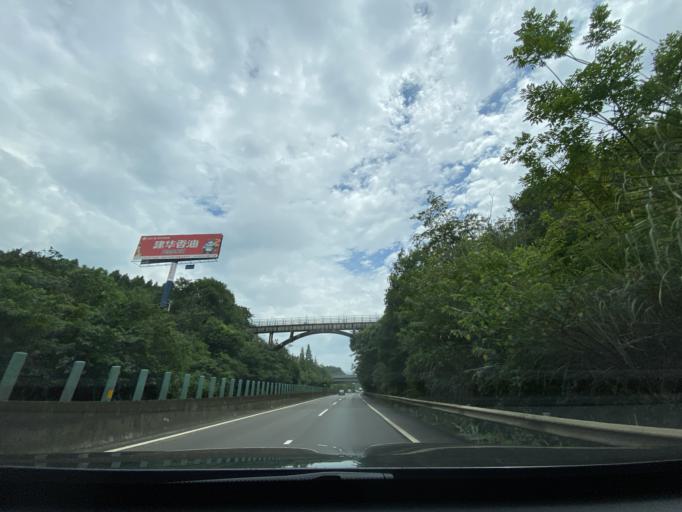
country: CN
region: Sichuan
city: Jiancheng
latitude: 30.3226
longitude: 104.5725
